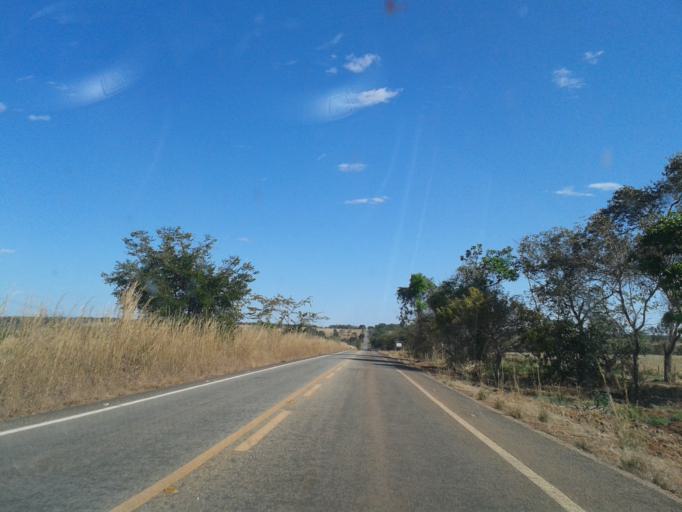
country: BR
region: Goias
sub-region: Mozarlandia
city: Mozarlandia
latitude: -14.5341
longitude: -50.4873
